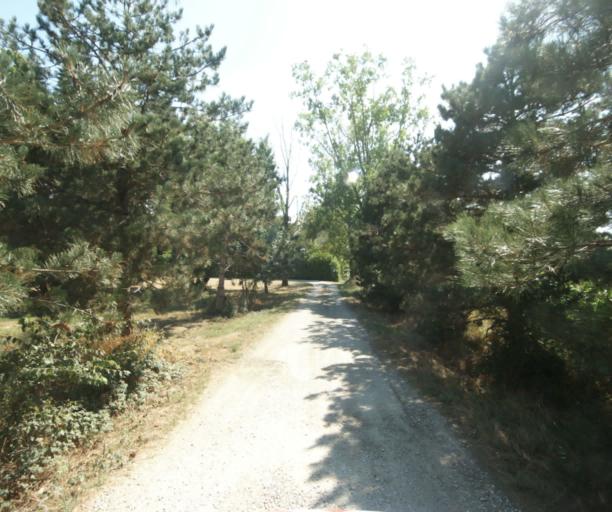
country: FR
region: Midi-Pyrenees
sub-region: Departement de la Haute-Garonne
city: Revel
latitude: 43.4868
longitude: 1.9788
